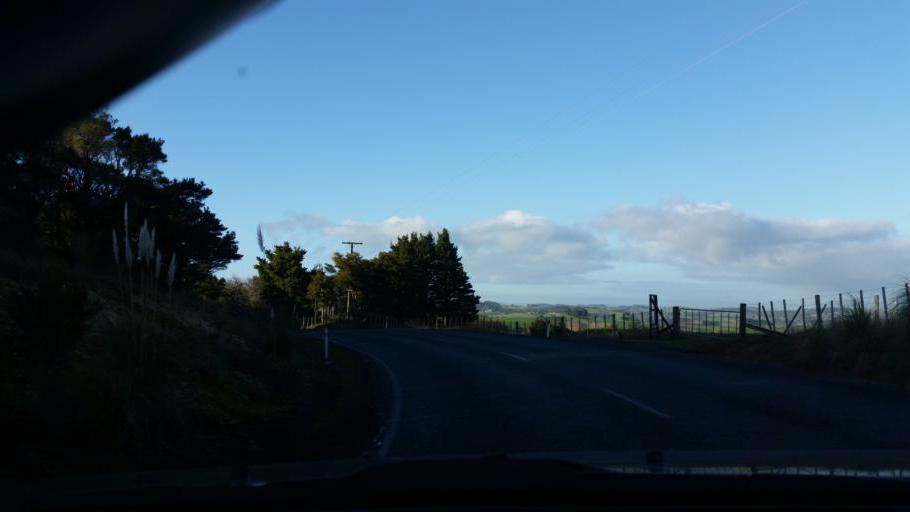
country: NZ
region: Auckland
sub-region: Auckland
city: Wellsford
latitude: -36.1224
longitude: 174.4578
